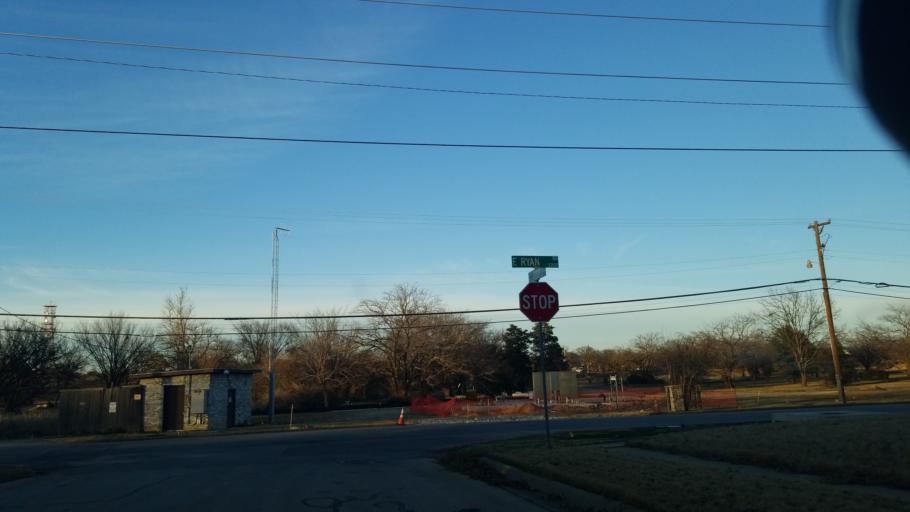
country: US
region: Texas
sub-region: Denton County
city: Corinth
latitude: 33.1613
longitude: -97.1096
